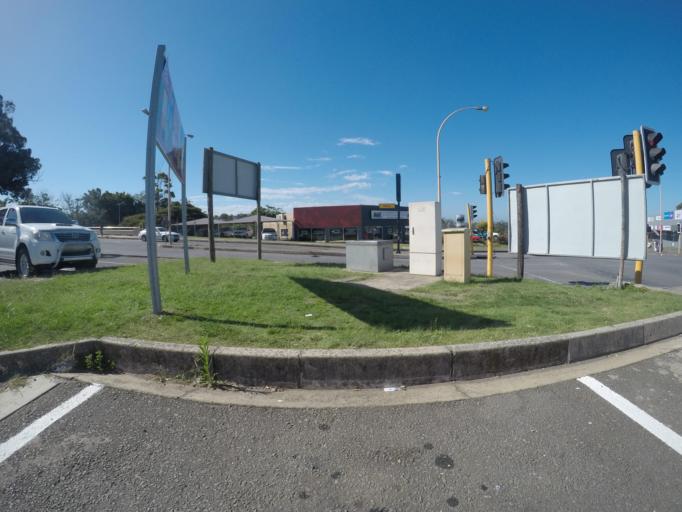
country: ZA
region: Eastern Cape
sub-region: Buffalo City Metropolitan Municipality
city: East London
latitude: -32.9832
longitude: 27.9196
